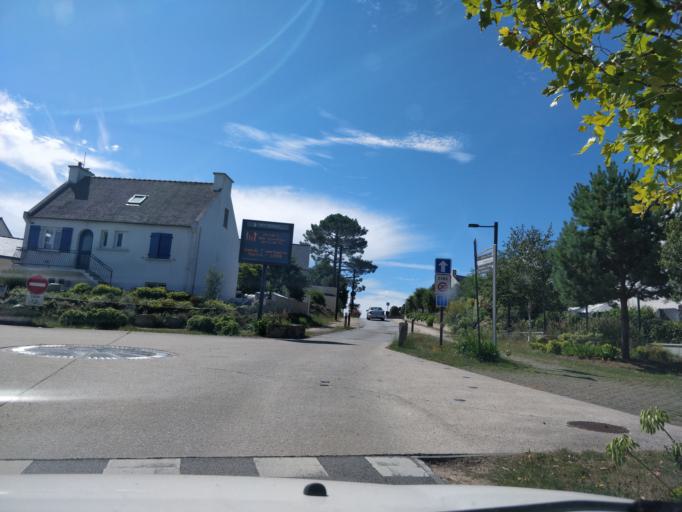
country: FR
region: Brittany
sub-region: Departement du Morbihan
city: Saint-Philibert
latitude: 47.5897
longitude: -3.0004
